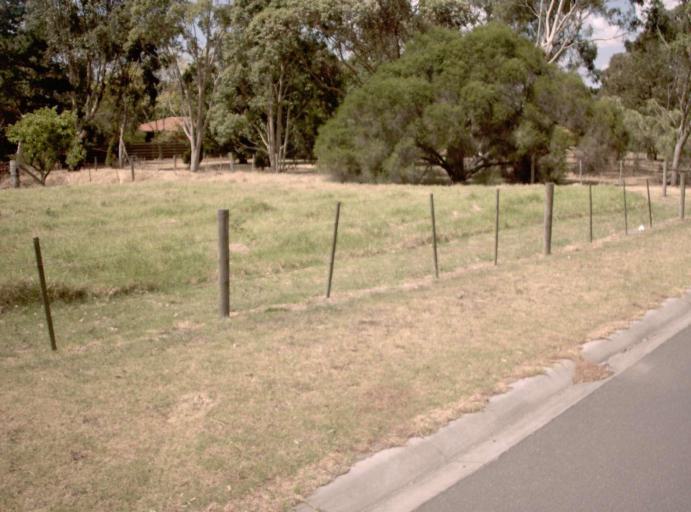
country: AU
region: Victoria
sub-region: Casey
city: Narre Warren South
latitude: -38.0303
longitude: 145.2831
